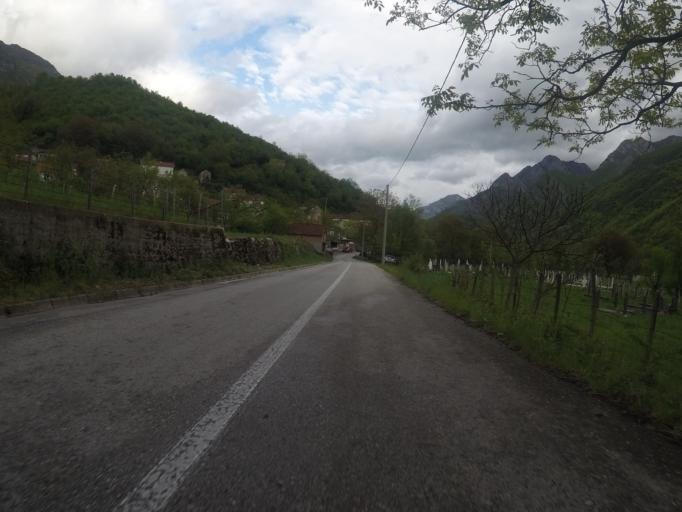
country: BA
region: Federation of Bosnia and Herzegovina
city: Siroki Brijeg
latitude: 43.5394
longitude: 17.5972
